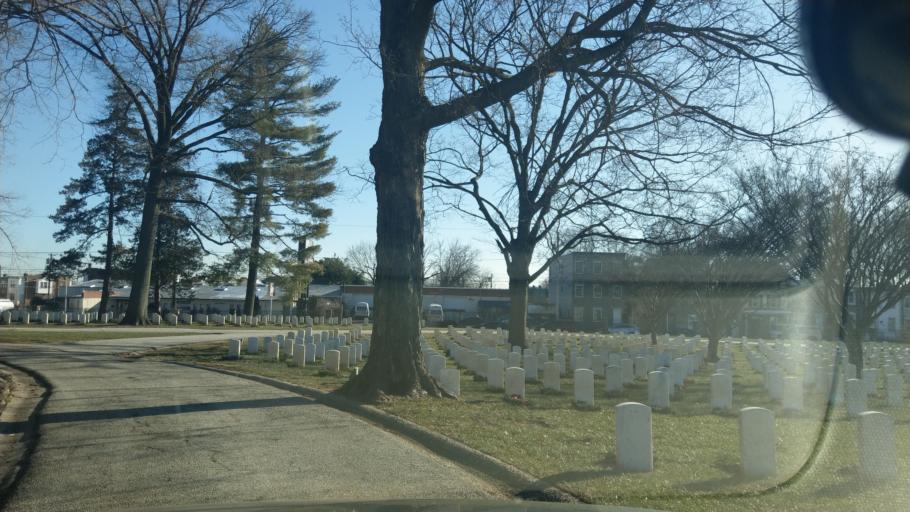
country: US
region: Pennsylvania
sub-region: Montgomery County
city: Wyncote
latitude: 40.0587
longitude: -75.1543
